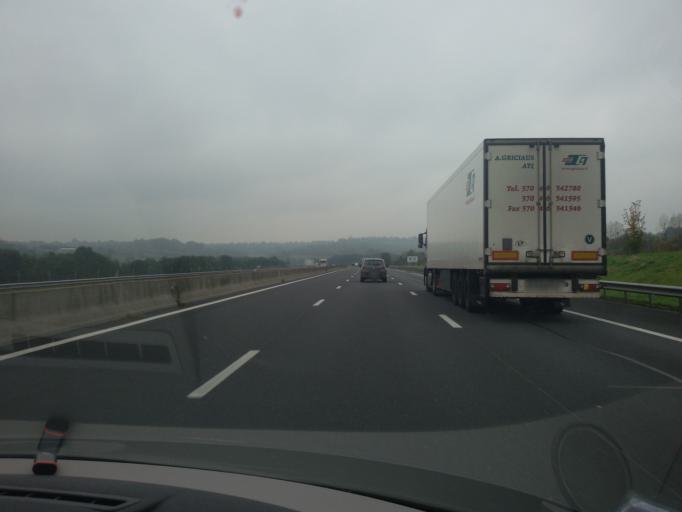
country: FR
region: Lower Normandy
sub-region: Departement du Calvados
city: Saint-Gatien-des-Bois
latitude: 49.2996
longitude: 0.2612
